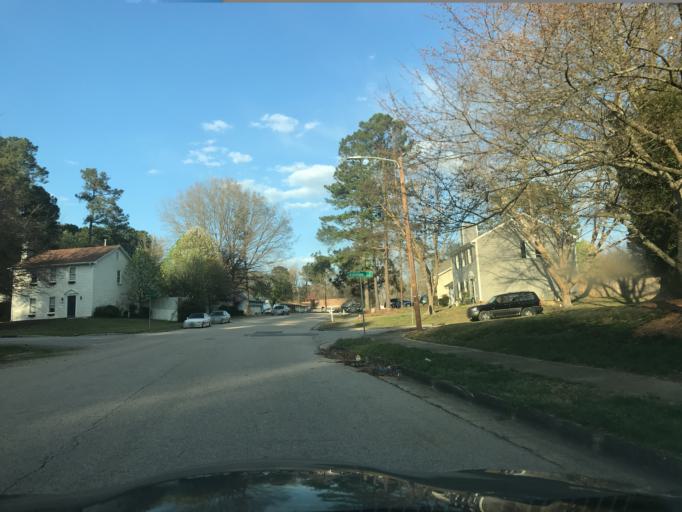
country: US
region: North Carolina
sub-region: Wake County
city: Raleigh
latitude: 35.8505
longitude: -78.5666
